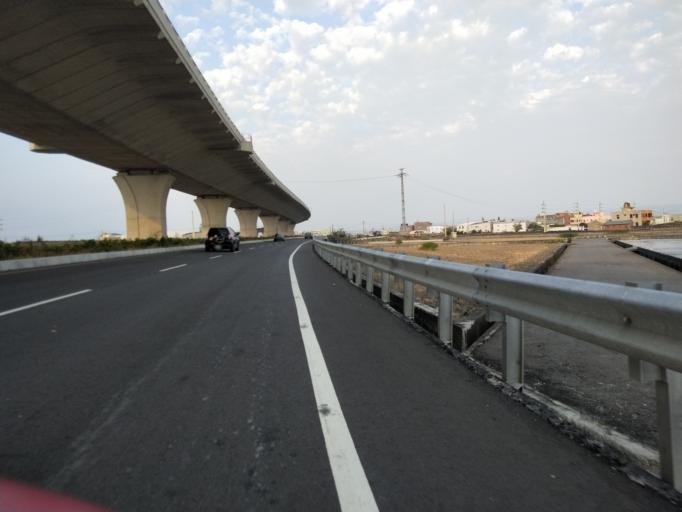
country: TW
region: Taiwan
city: Fengyuan
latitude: 24.4249
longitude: 120.6219
